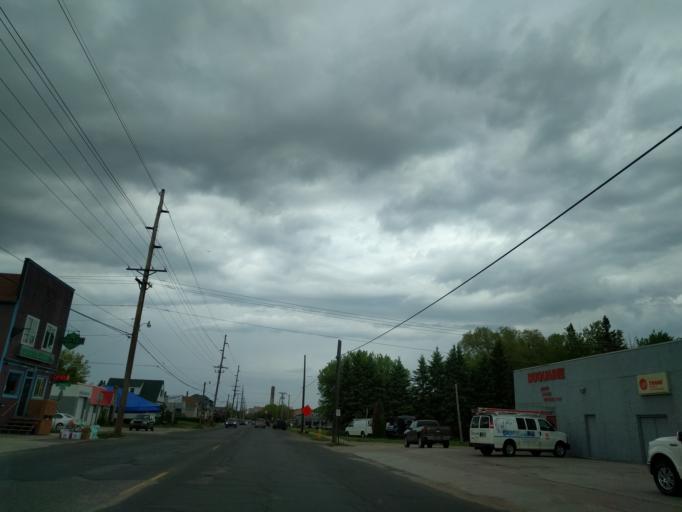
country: US
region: Michigan
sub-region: Marquette County
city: Marquette
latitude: 46.5617
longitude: -87.3961
